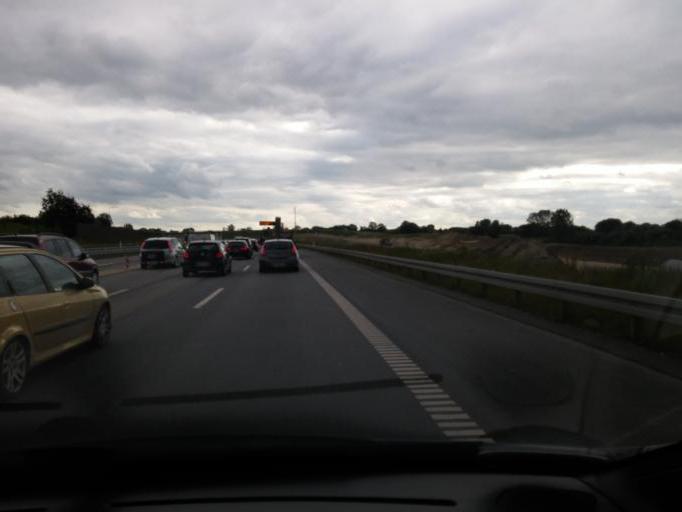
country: DK
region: Zealand
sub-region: Solrod Kommune
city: Solrod Strand
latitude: 55.5398
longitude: 12.2047
